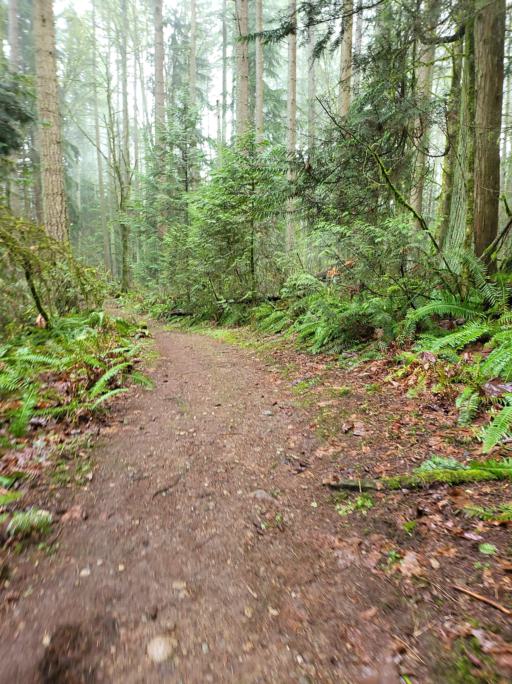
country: US
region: Washington
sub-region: King County
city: Newcastle
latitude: 47.5270
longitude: -122.1385
